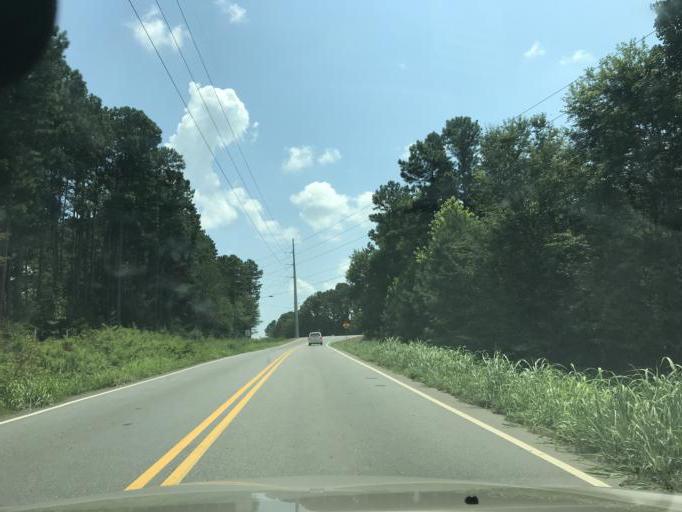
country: US
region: Georgia
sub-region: Forsyth County
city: Cumming
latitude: 34.3071
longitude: -84.2169
